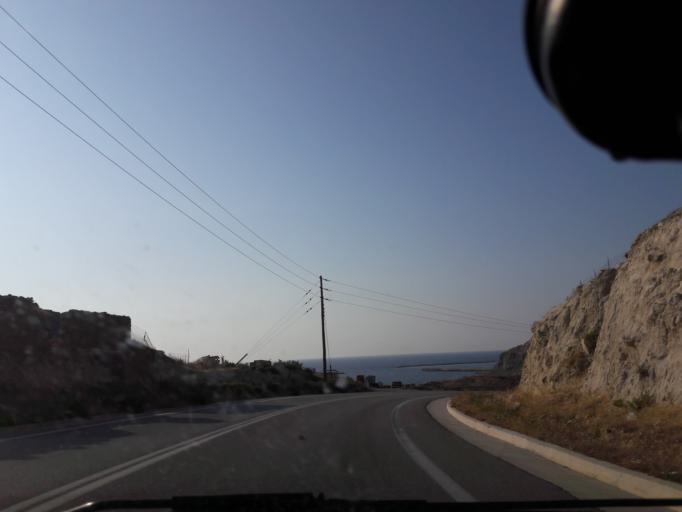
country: GR
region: North Aegean
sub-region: Nomos Lesvou
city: Myrina
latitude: 39.8624
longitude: 25.0559
